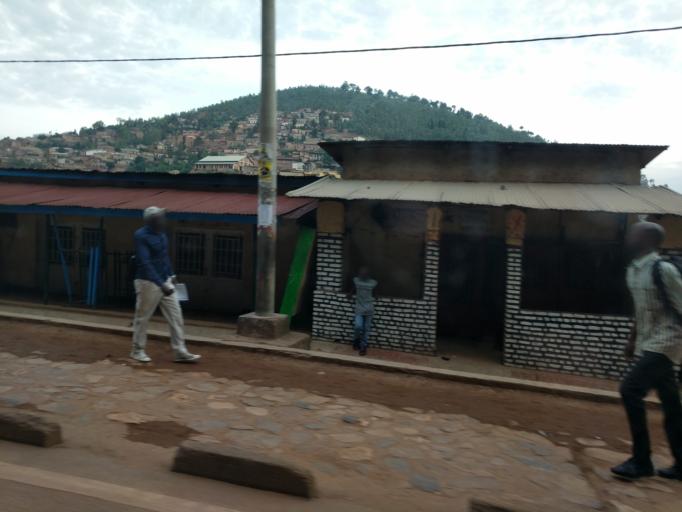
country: RW
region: Kigali
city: Kigali
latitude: -1.9429
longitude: 30.0411
